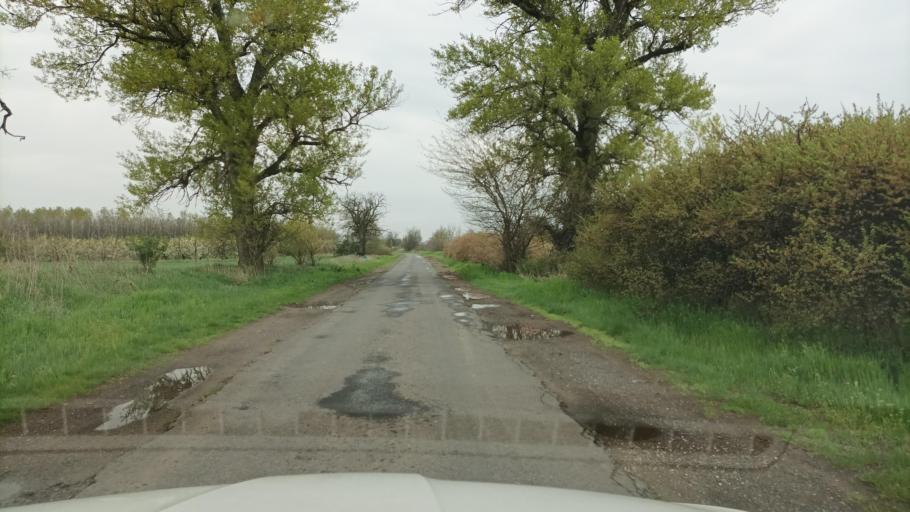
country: HU
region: Pest
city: Nagykoros
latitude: 46.9976
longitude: 19.8008
